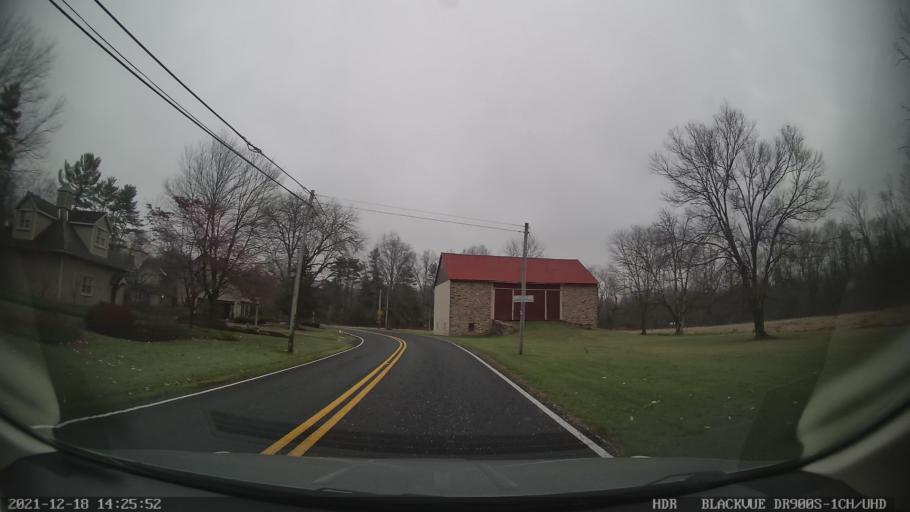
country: US
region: Pennsylvania
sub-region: Berks County
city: Oley
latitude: 40.4118
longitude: -75.7393
